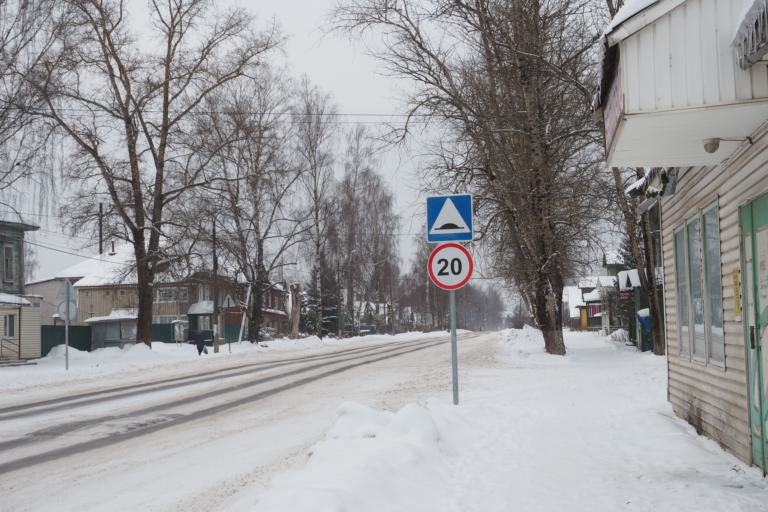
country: RU
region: Tverskaya
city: Ves'yegonsk
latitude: 58.6634
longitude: 37.2618
